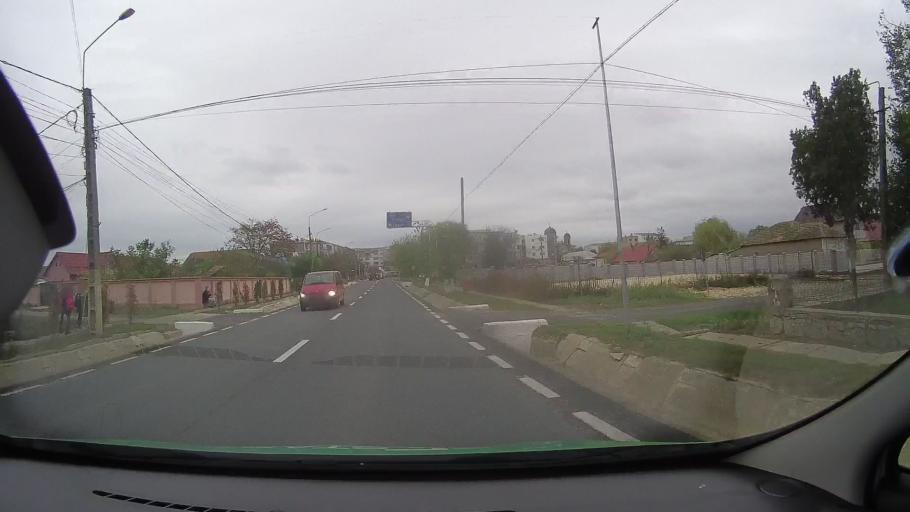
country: RO
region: Constanta
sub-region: Comuna Mihail Kogalniceanu
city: Mihail Kogalniceanu
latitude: 44.3673
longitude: 28.4593
